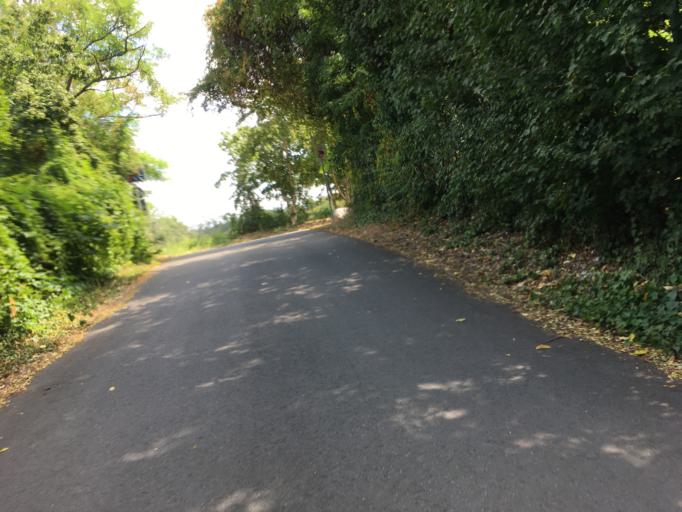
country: DE
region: Rheinland-Pfalz
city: Altrip
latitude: 49.4280
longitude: 8.4679
